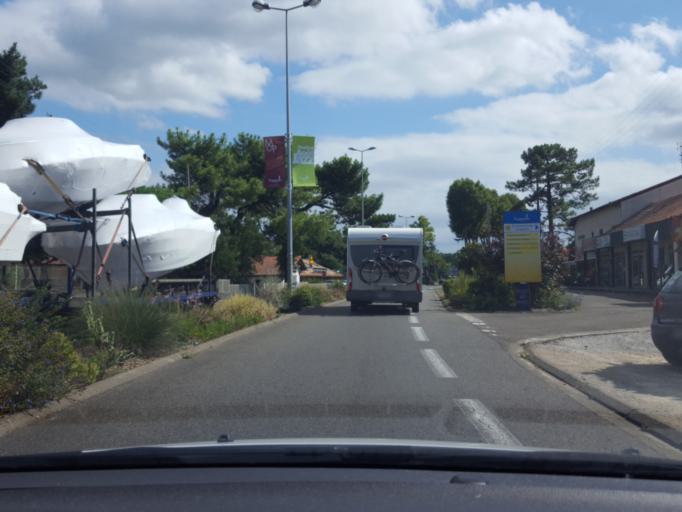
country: FR
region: Aquitaine
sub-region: Departement des Landes
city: Capbreton
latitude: 43.6429
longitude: -1.4261
